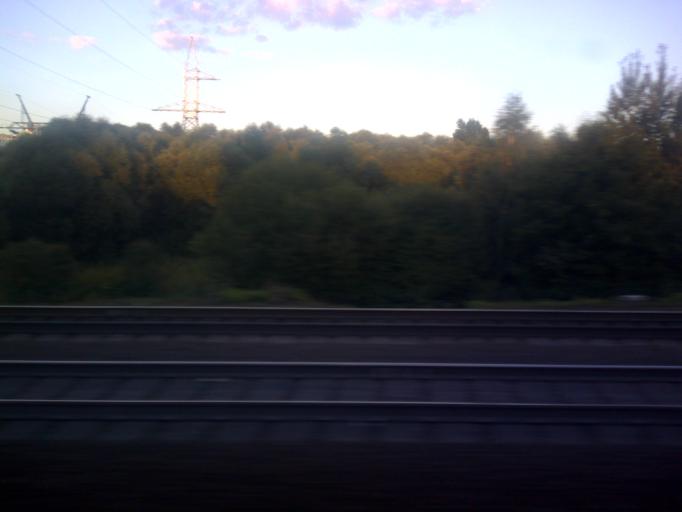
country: RU
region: Moscow
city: Orekhovo-Borisovo Severnoye
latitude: 55.6358
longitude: 37.6867
